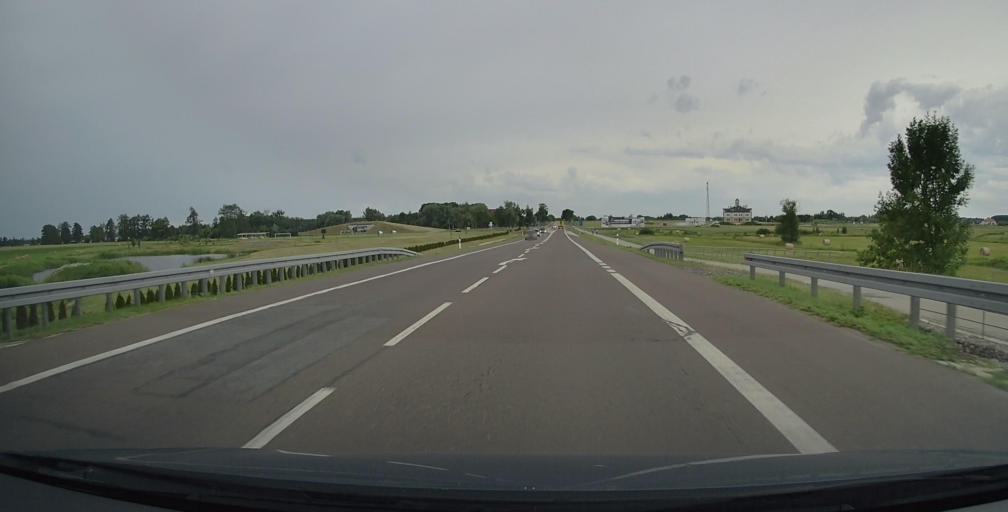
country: PL
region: Lublin Voivodeship
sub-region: Powiat bialski
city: Terespol
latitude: 52.0573
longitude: 23.5707
